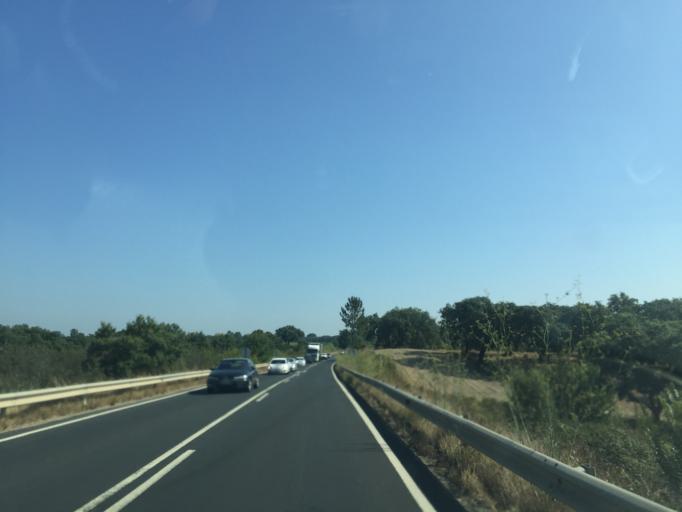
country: PT
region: Santarem
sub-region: Alpiarca
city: Alpiarca
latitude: 39.2769
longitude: -8.5450
